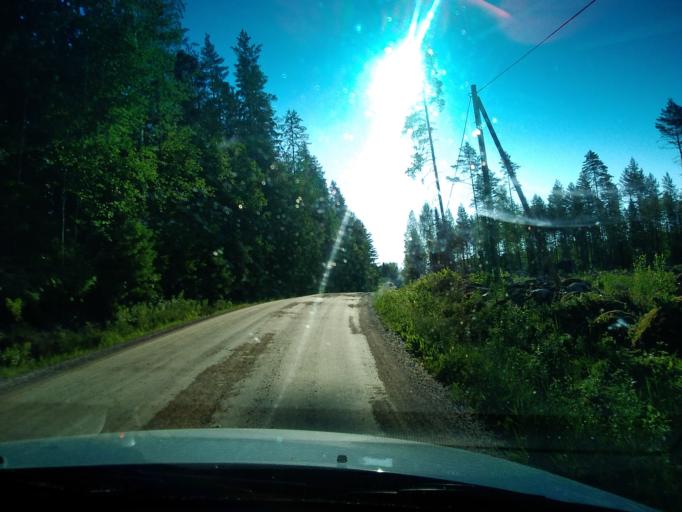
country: FI
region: Haeme
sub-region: Forssa
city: Tammela
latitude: 60.7600
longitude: 23.7716
